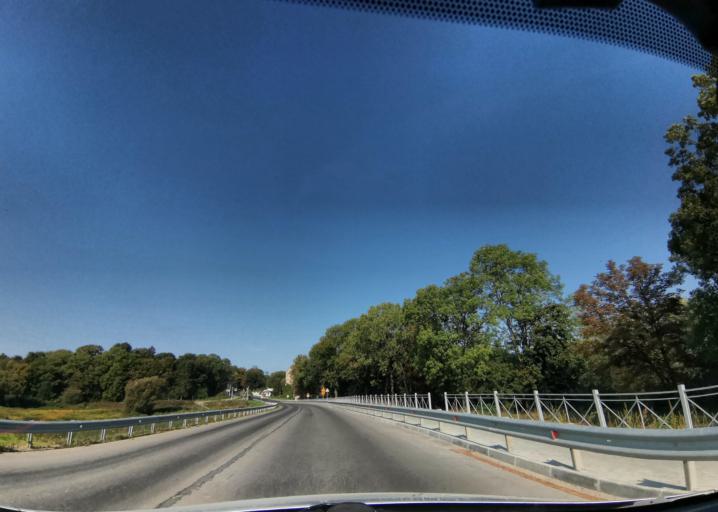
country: RU
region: Kaliningrad
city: Chernyakhovsk
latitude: 54.6590
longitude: 21.8099
